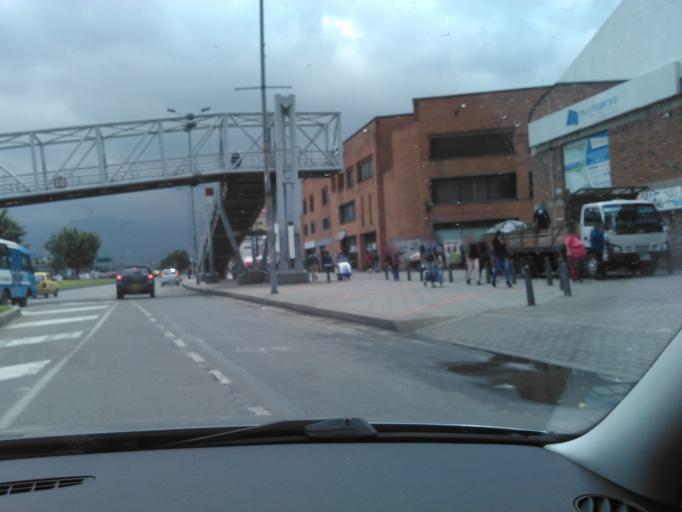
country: CO
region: Bogota D.C.
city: Bogota
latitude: 4.6283
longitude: -74.1201
